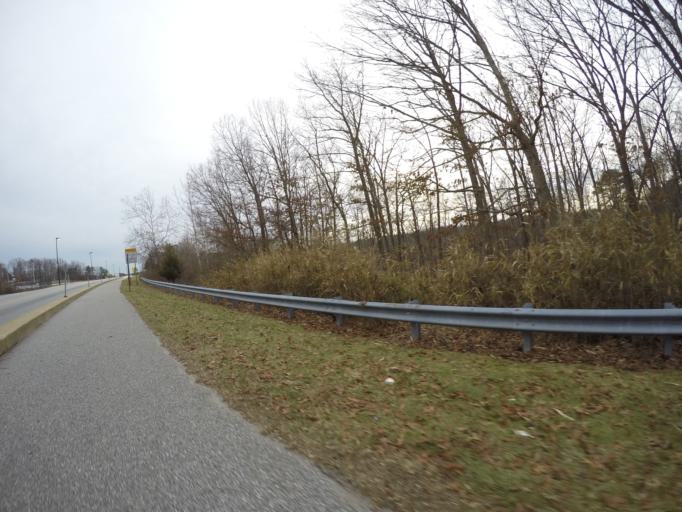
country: US
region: Maryland
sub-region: Howard County
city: Elkridge
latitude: 39.1888
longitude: -76.6908
